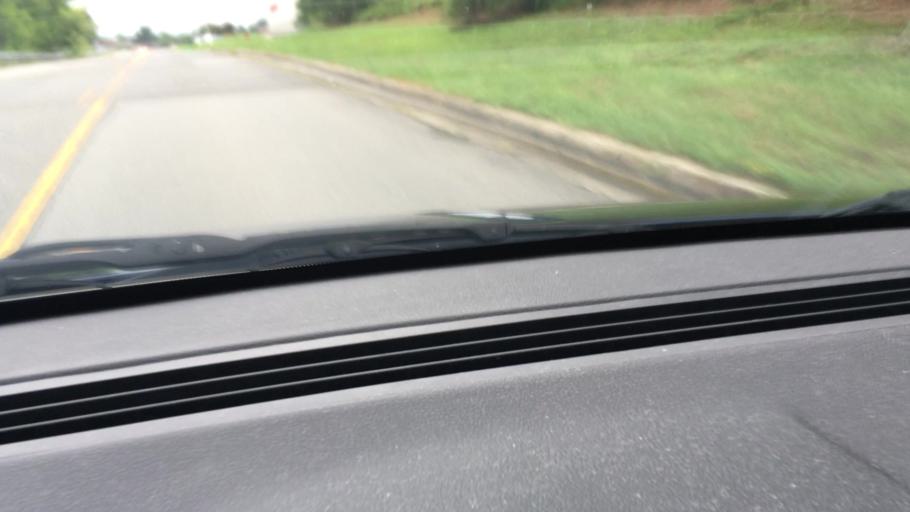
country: US
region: Alabama
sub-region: Tuscaloosa County
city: Tuscaloosa
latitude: 33.1912
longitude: -87.5192
